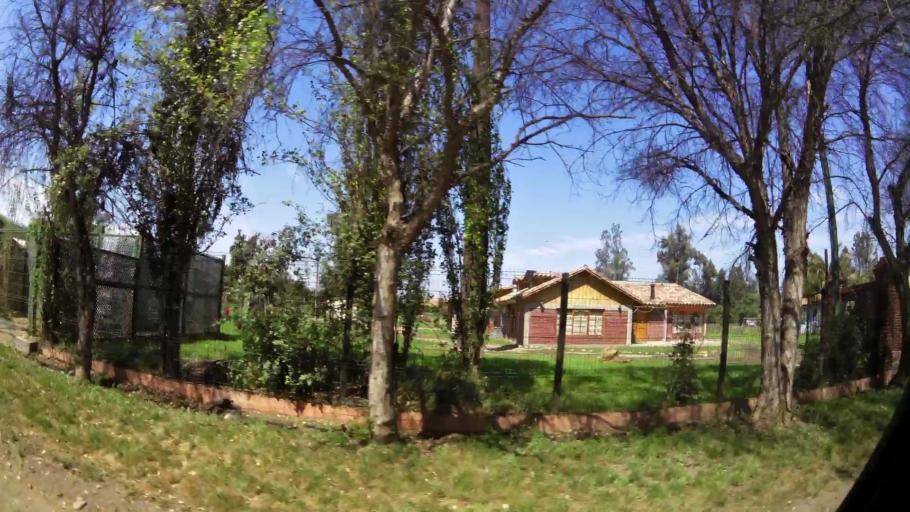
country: CL
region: Santiago Metropolitan
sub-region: Provincia de Talagante
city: Talagante
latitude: -33.6482
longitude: -70.9042
